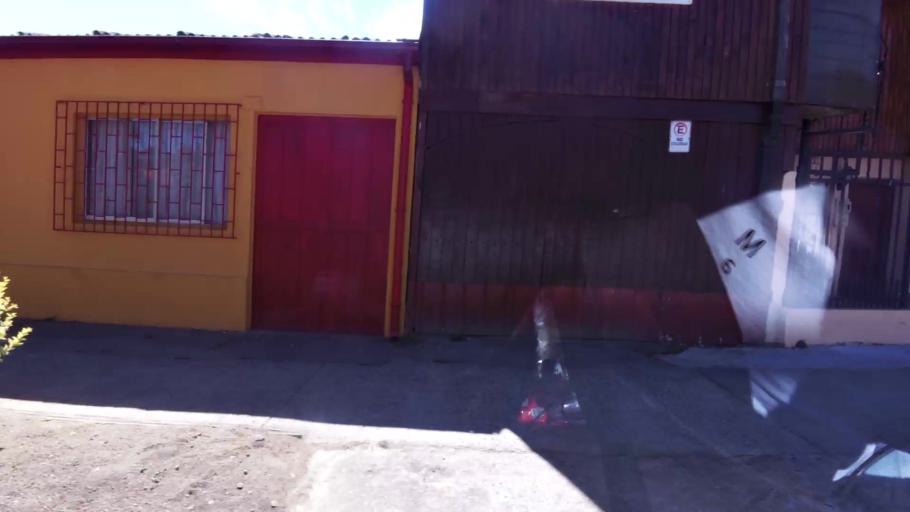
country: CL
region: Biobio
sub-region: Provincia de Concepcion
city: Penco
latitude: -36.7379
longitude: -72.9893
